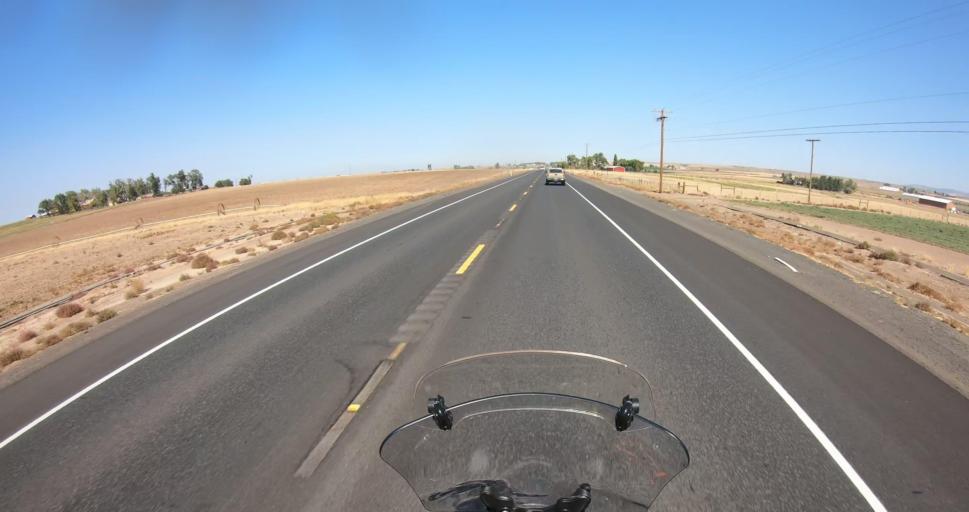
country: US
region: Oregon
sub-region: Jefferson County
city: Culver
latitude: 44.5405
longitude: -121.1687
